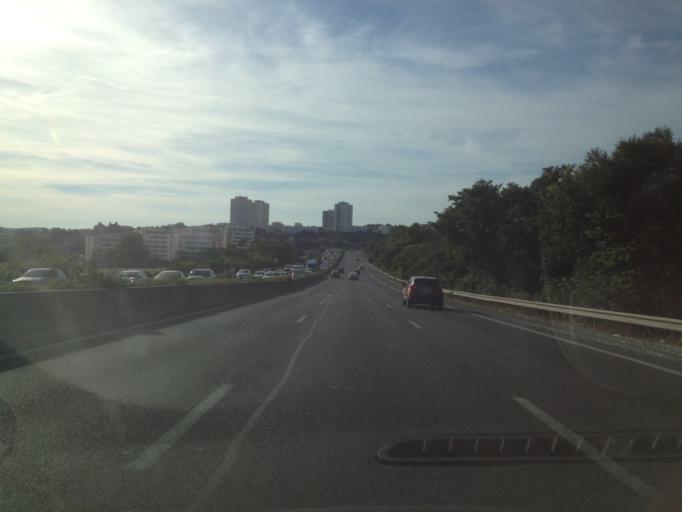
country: FR
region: Provence-Alpes-Cote d'Azur
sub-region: Departement des Bouches-du-Rhone
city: Marseille 14
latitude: 43.3486
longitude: 5.3703
